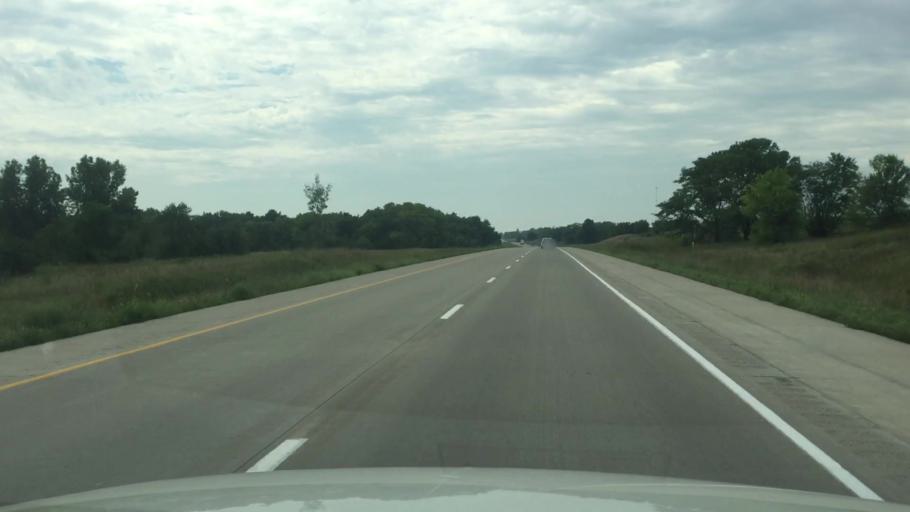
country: US
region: Iowa
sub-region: Decatur County
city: Lamoni
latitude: 40.6090
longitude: -93.9049
